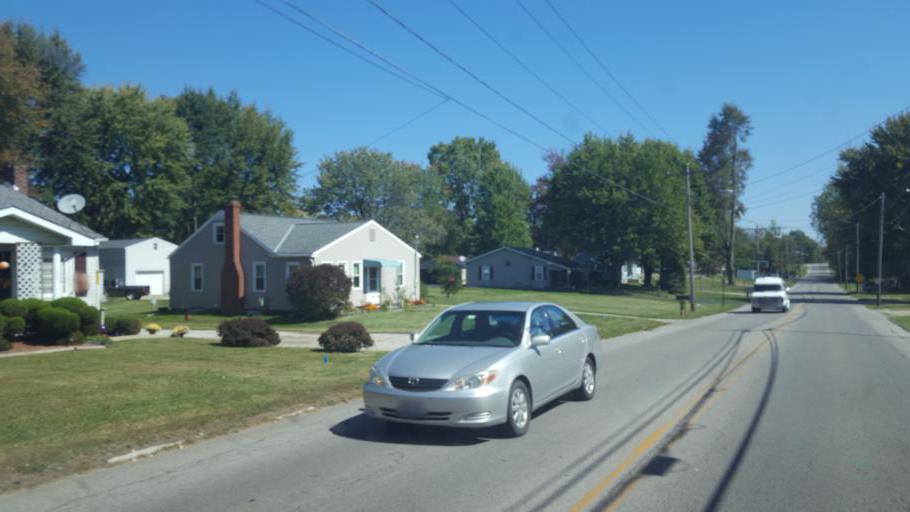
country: US
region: Ohio
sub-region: Crawford County
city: Galion
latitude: 40.7376
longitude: -82.7727
